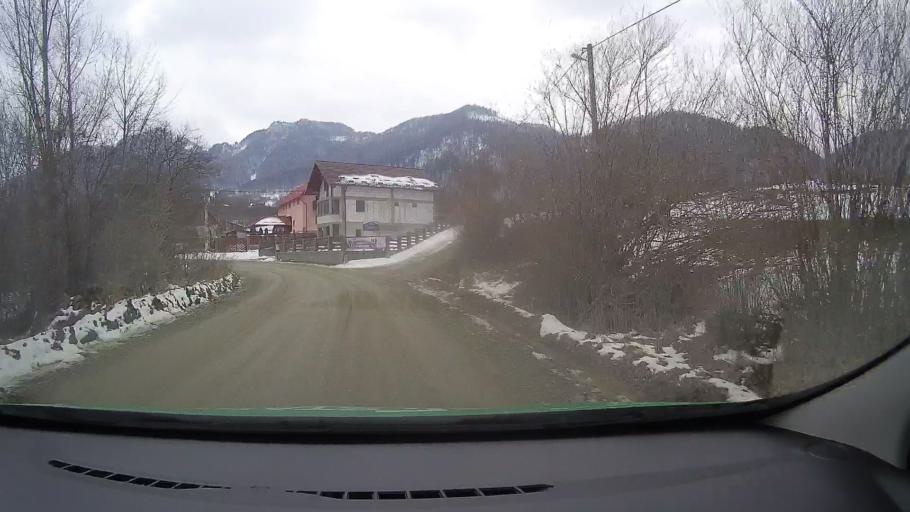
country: RO
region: Brasov
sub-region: Comuna Zarnesti
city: Zarnesti
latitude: 45.5452
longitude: 25.3222
